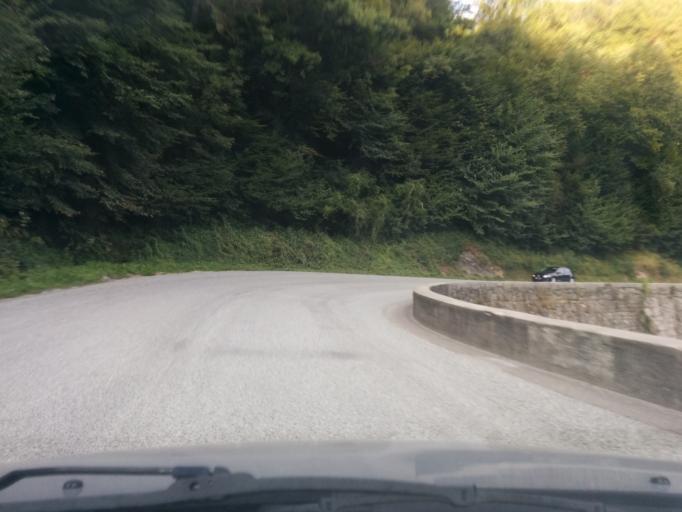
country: FR
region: Rhone-Alpes
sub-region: Departement de la Savoie
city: Saint-Beron
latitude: 45.4757
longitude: 5.7330
